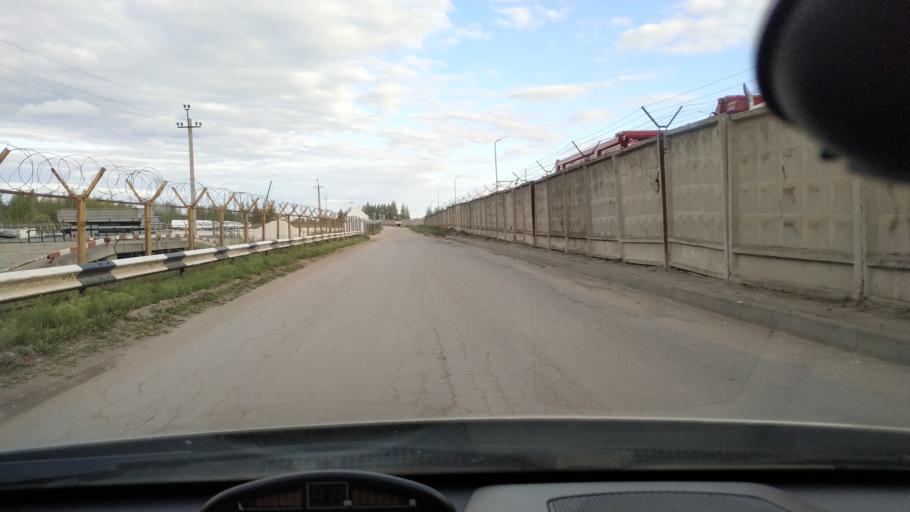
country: RU
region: Rjazan
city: Polyany
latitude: 54.5782
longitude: 39.8401
